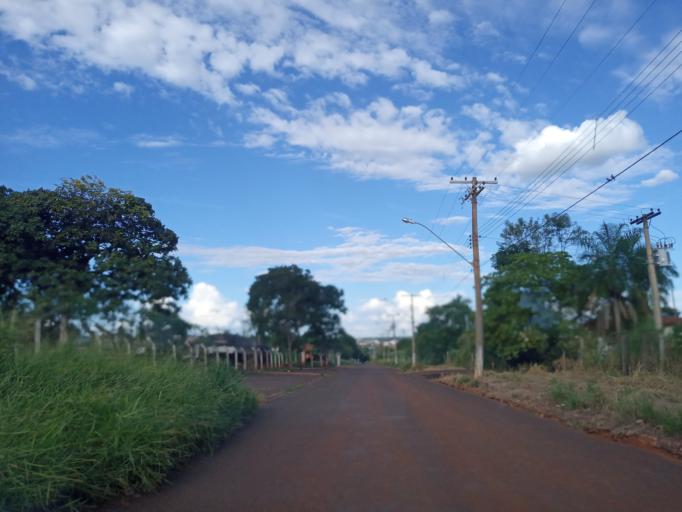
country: BR
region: Minas Gerais
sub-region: Ituiutaba
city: Ituiutaba
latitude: -18.9644
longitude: -49.4951
